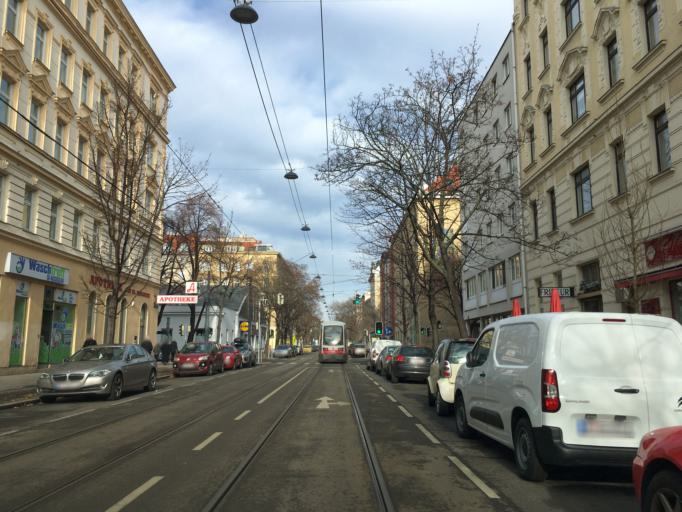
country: AT
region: Vienna
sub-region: Wien Stadt
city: Vienna
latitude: 48.2331
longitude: 16.3660
